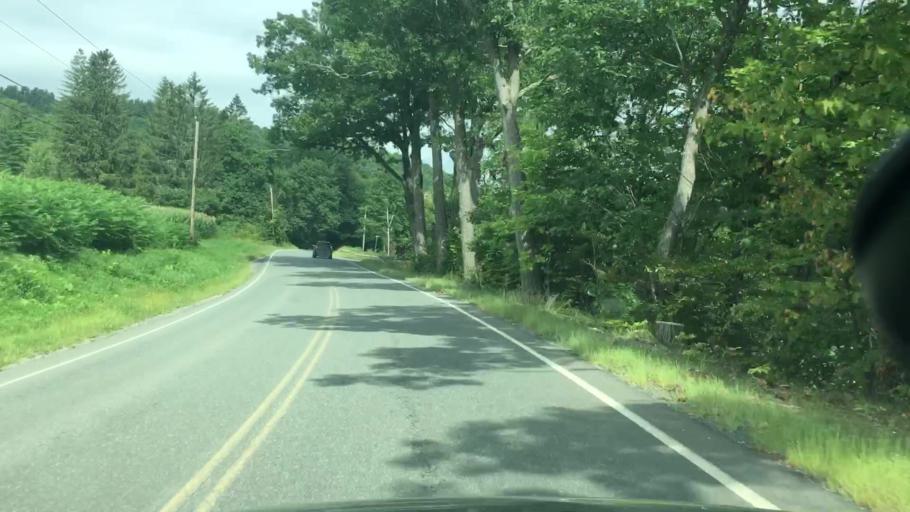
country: US
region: Massachusetts
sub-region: Franklin County
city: Colrain
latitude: 42.6889
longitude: -72.6914
